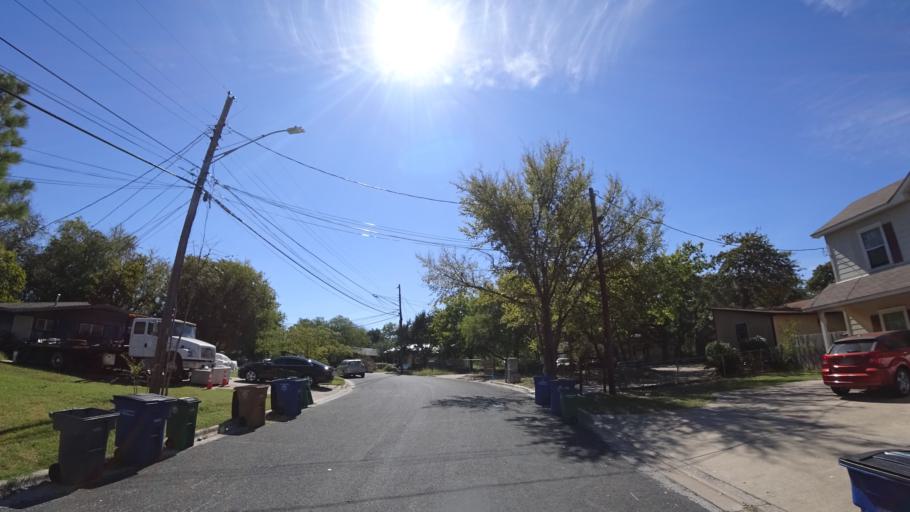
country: US
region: Texas
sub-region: Travis County
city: Austin
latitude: 30.2795
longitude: -97.6770
